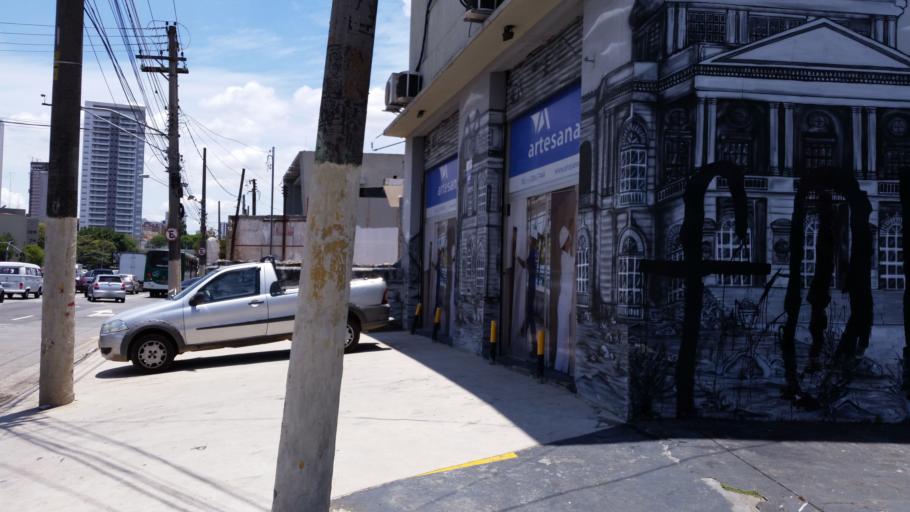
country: BR
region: Sao Paulo
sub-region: Sao Paulo
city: Sao Paulo
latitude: -23.5867
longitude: -46.6188
